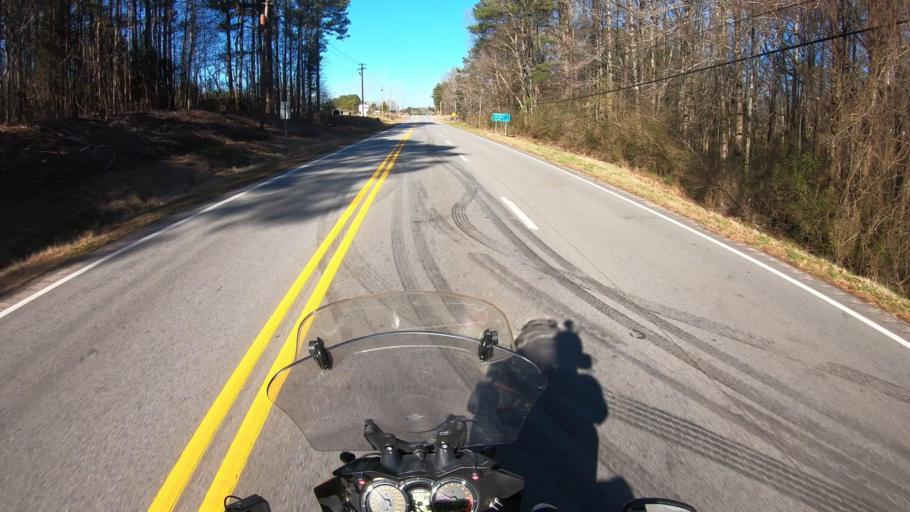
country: US
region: Alabama
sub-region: Cleburne County
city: Heflin
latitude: 33.6575
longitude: -85.5782
